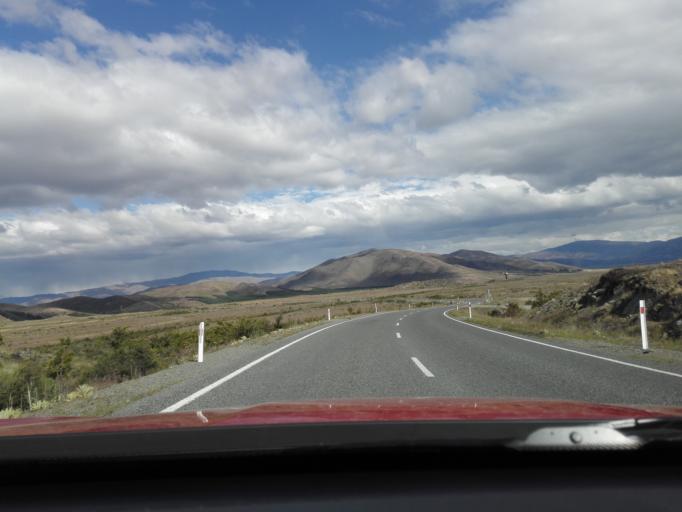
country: NZ
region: Canterbury
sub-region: Timaru District
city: Pleasant Point
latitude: -44.1975
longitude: 170.2475
